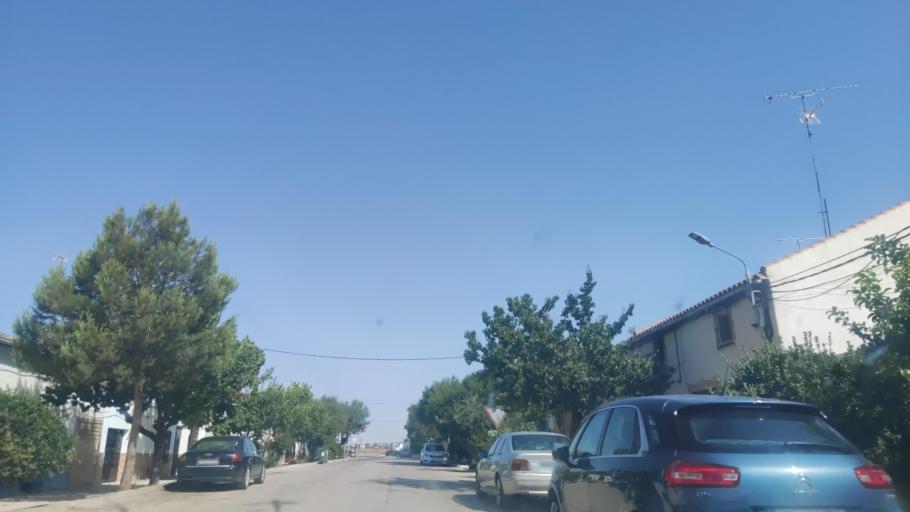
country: ES
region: Castille-La Mancha
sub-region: Provincia de Albacete
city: La Gineta
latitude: 39.1164
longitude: -1.9996
